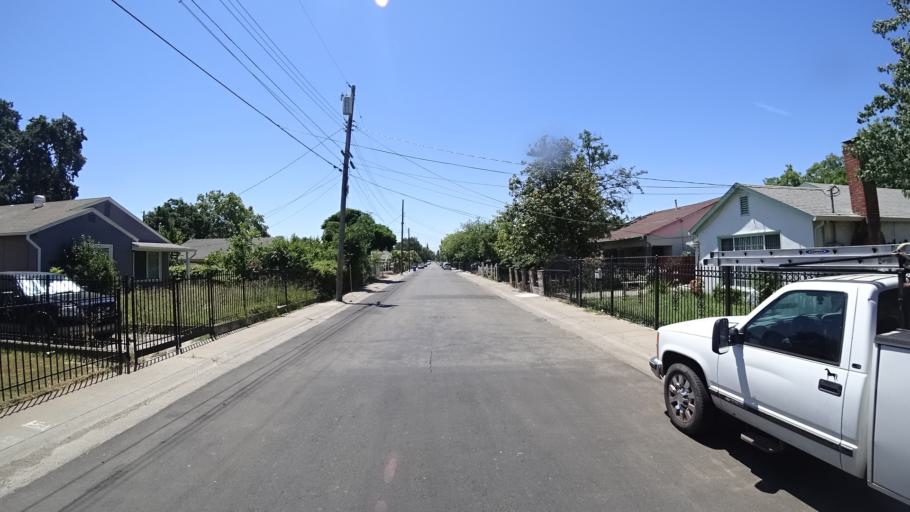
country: US
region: California
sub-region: Sacramento County
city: Parkway
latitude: 38.5371
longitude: -121.4682
